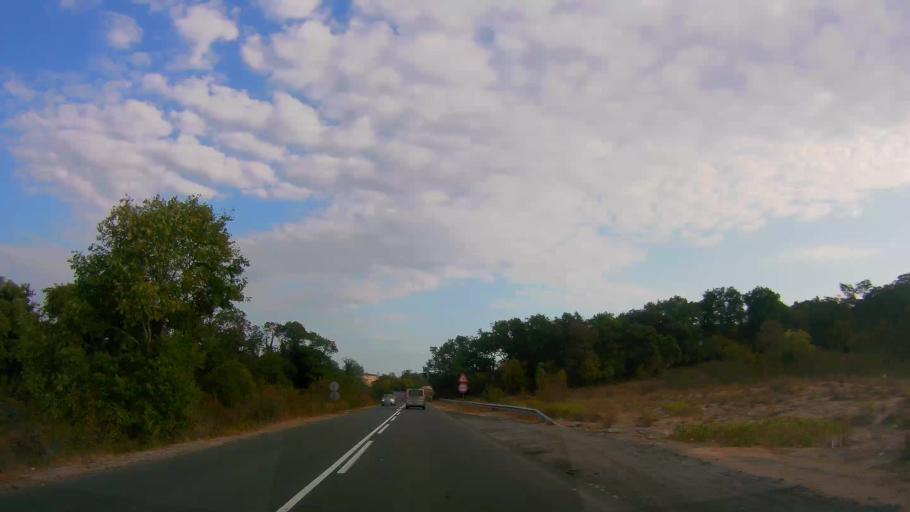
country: BG
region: Burgas
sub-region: Obshtina Primorsko
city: Primorsko
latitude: 42.3246
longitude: 27.7304
